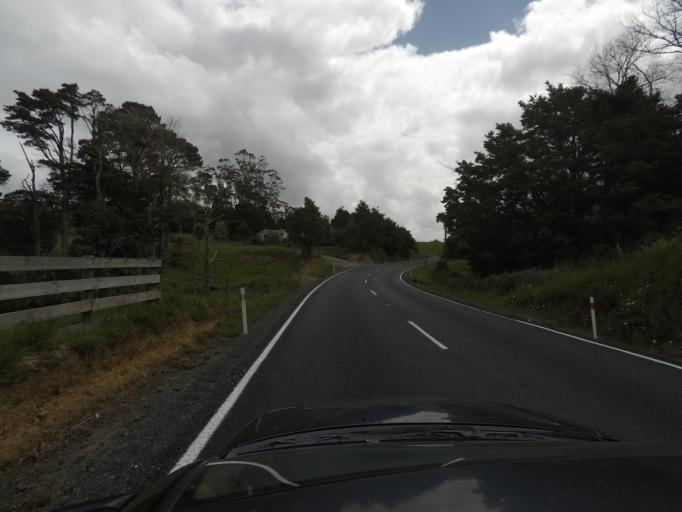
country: NZ
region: Auckland
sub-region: Auckland
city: Parakai
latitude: -36.5030
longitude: 174.5170
